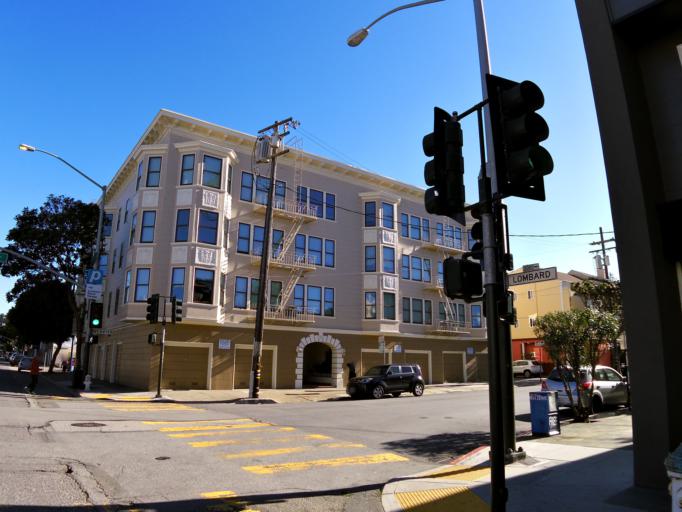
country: US
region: California
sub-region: San Francisco County
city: San Francisco
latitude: 37.8000
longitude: -122.4346
